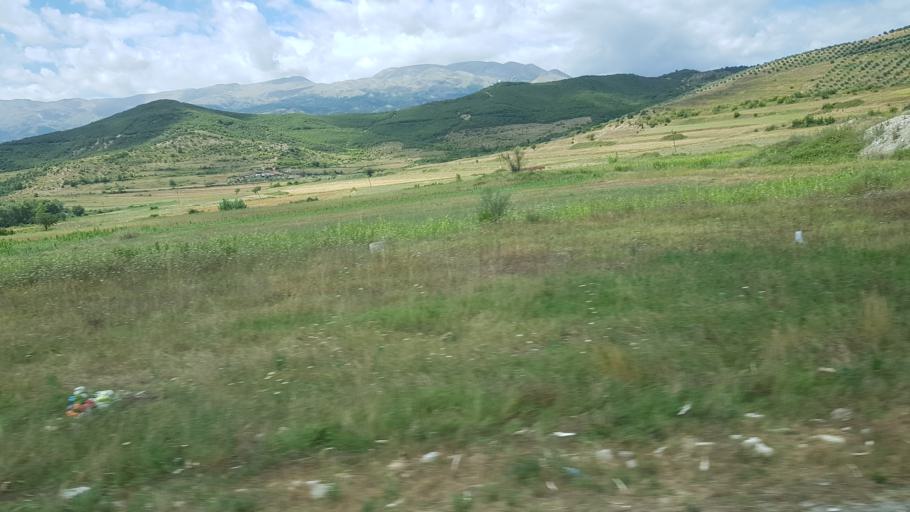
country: AL
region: Gjirokaster
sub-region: Rrethi i Tepelenes
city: Krahes
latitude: 40.4231
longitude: 19.8569
